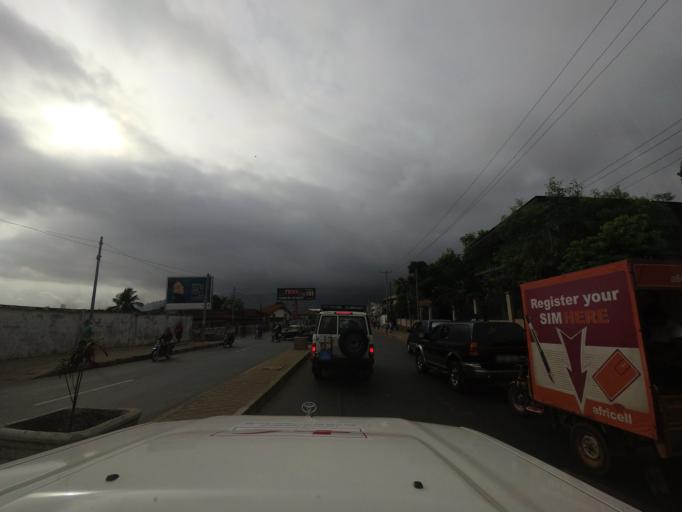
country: SL
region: Western Area
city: Freetown
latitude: 8.4823
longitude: -13.2574
